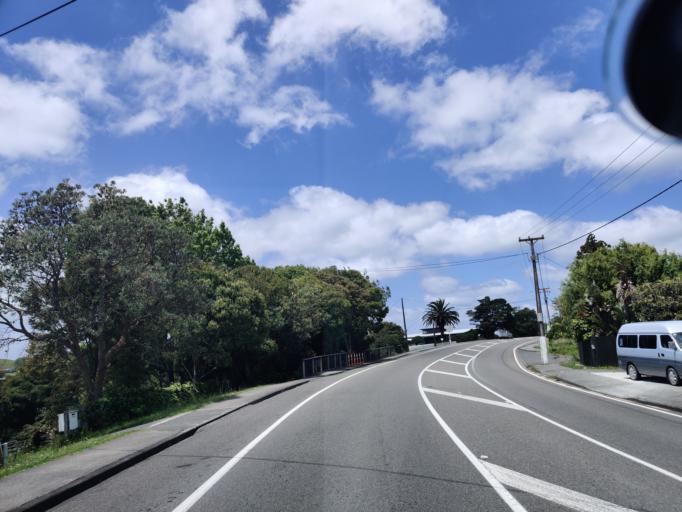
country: NZ
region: Auckland
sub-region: Auckland
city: Wellsford
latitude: -36.2903
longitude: 174.5238
